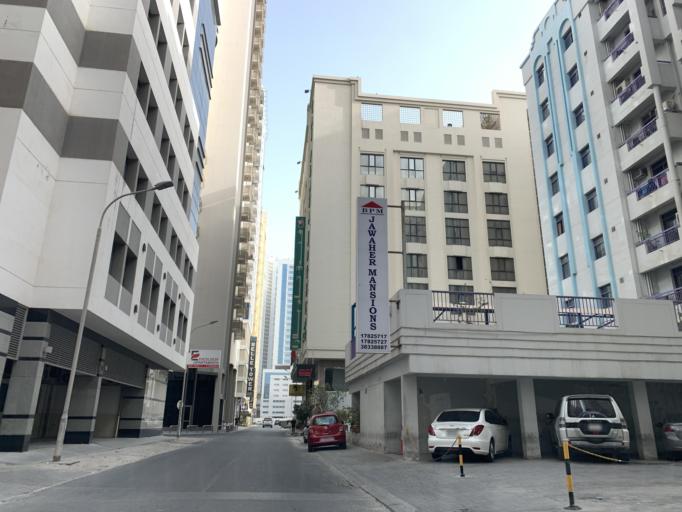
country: BH
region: Manama
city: Manama
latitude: 26.2193
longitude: 50.6078
